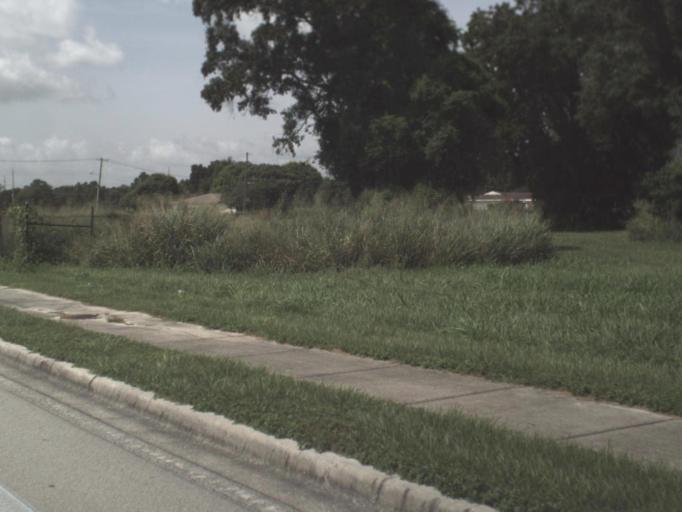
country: US
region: Florida
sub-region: Polk County
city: Jan-Phyl Village
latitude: 28.0051
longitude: -81.7520
